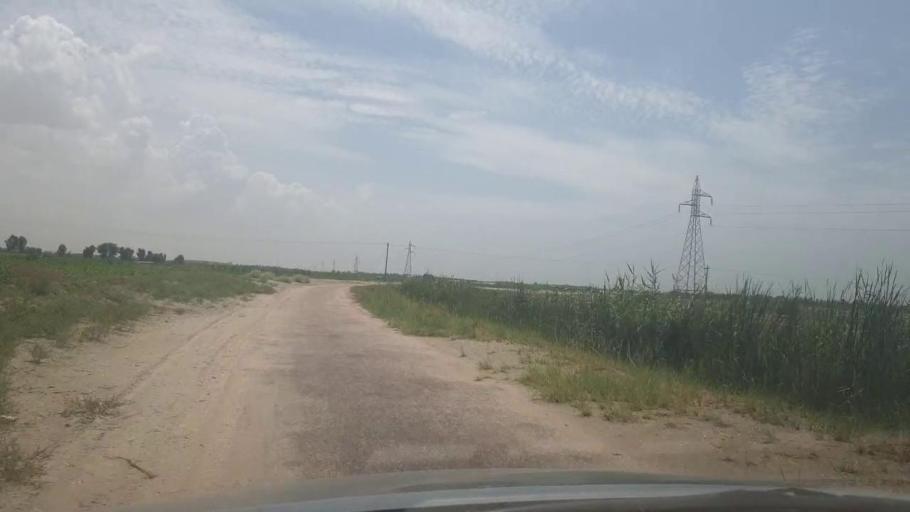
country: PK
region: Sindh
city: Kot Diji
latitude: 27.3897
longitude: 68.7043
